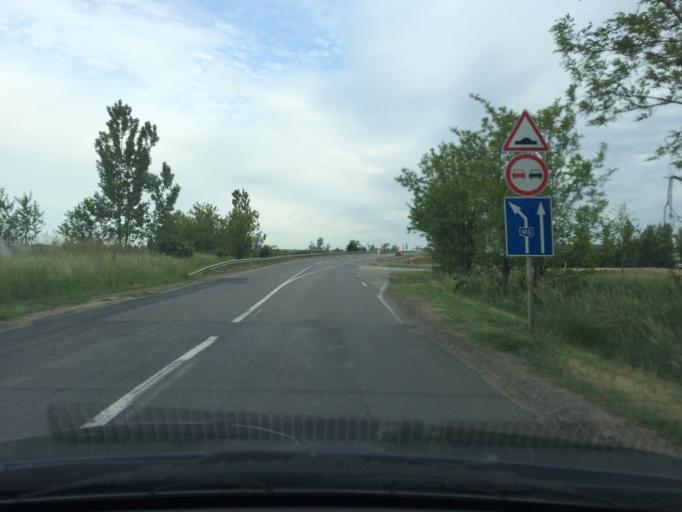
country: HU
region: Hajdu-Bihar
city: Hajdunanas
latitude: 47.8865
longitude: 21.4137
